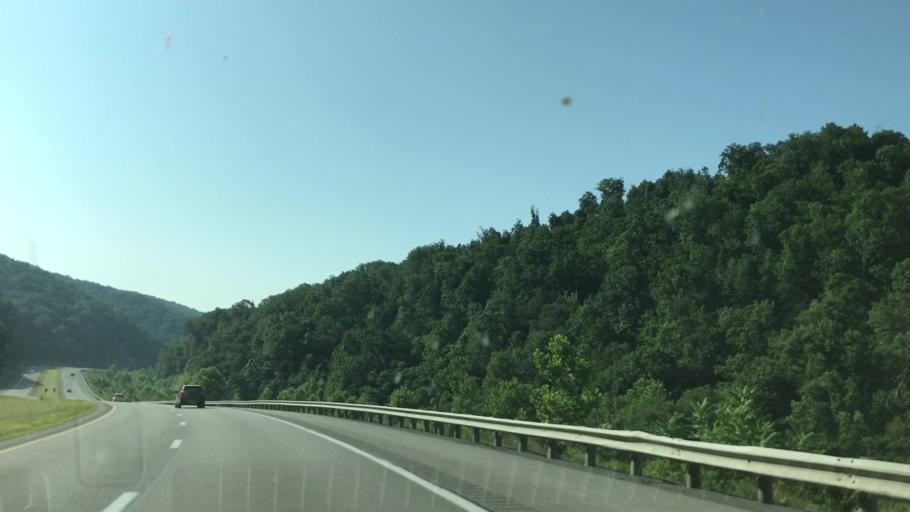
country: US
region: West Virginia
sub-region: Braxton County
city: Sutton
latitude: 38.5702
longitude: -80.7377
